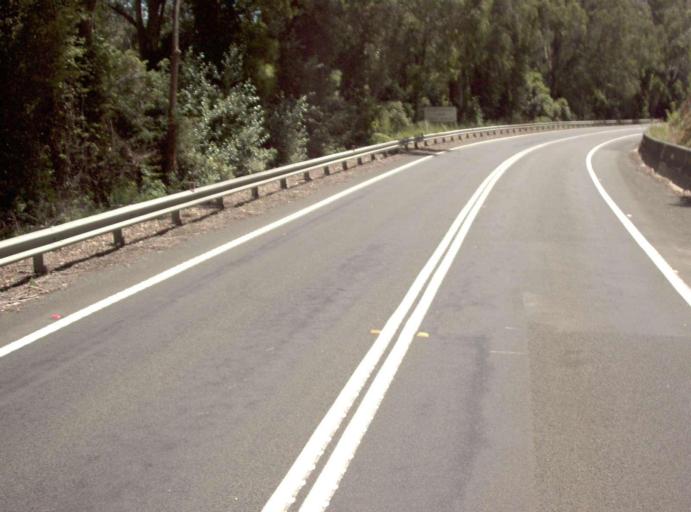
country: AU
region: New South Wales
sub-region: Bombala
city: Bombala
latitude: -37.6082
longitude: 148.8989
